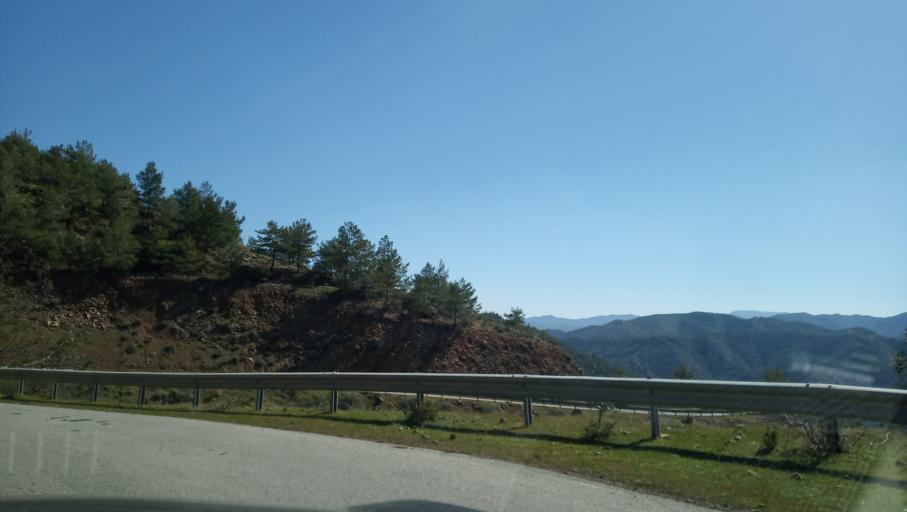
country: CY
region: Lefkosia
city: Lefka
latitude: 35.0813
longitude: 32.7762
